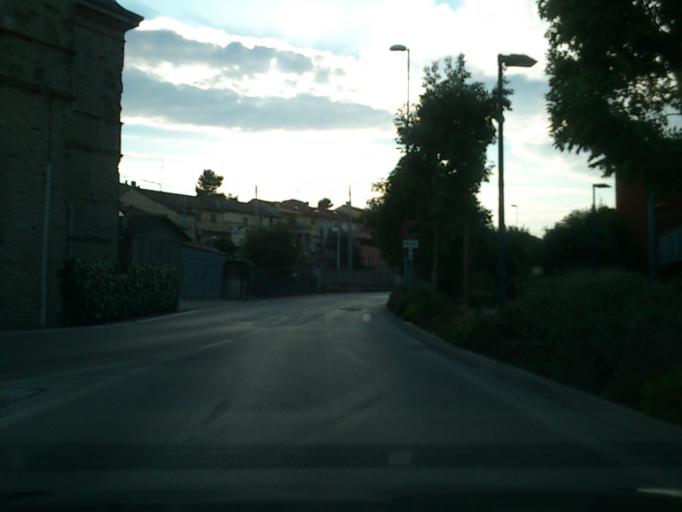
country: IT
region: The Marches
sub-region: Provincia di Pesaro e Urbino
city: Fano
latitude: 43.8440
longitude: 13.0233
